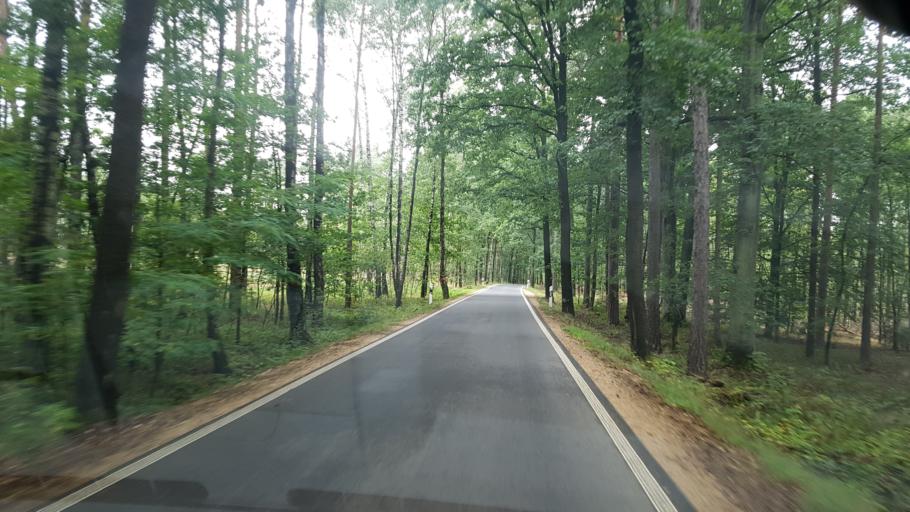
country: DE
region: Saxony
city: Konigshain
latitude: 51.2200
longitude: 14.8349
